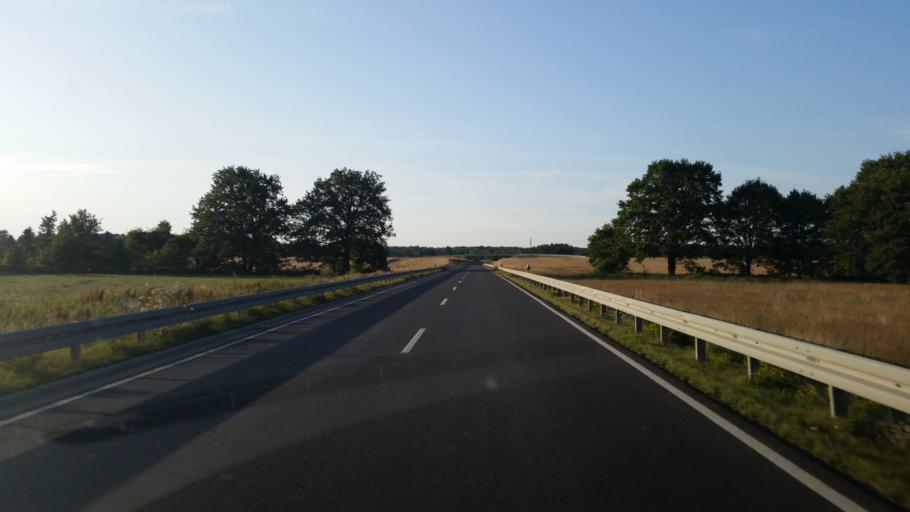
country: DE
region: Saxony
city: Bernsdorf
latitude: 51.3665
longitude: 14.0806
